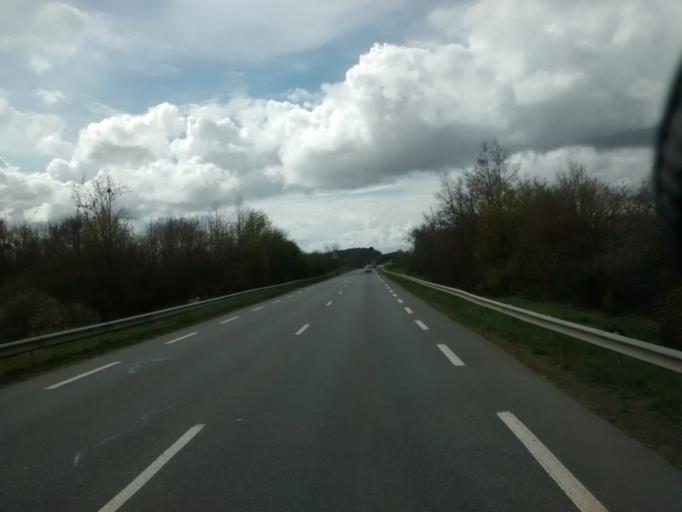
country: FR
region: Brittany
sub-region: Departement d'Ille-et-Vilaine
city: Chavagne
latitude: 48.0614
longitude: -1.7644
